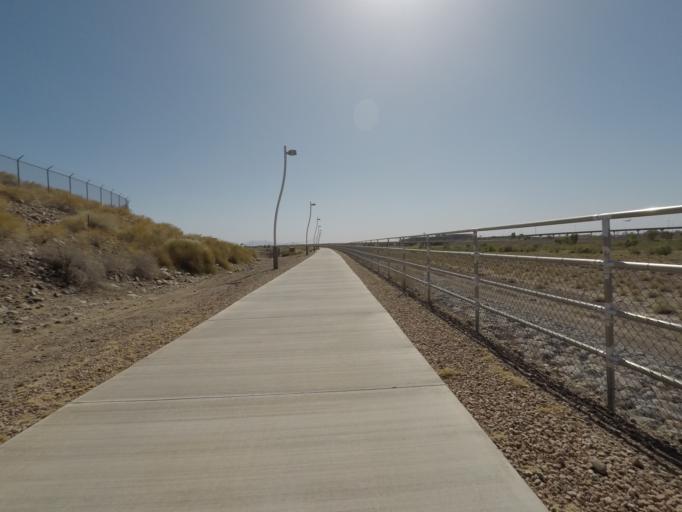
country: US
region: Arizona
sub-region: Maricopa County
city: Tempe Junction
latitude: 33.4339
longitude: -111.9706
